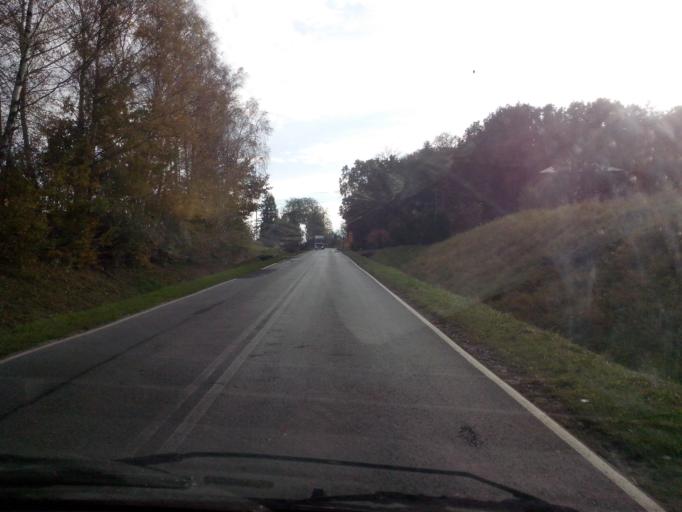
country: PL
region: Subcarpathian Voivodeship
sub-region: Powiat ropczycko-sedziszowski
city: Wielopole Skrzynskie
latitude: 49.9382
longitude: 21.6165
